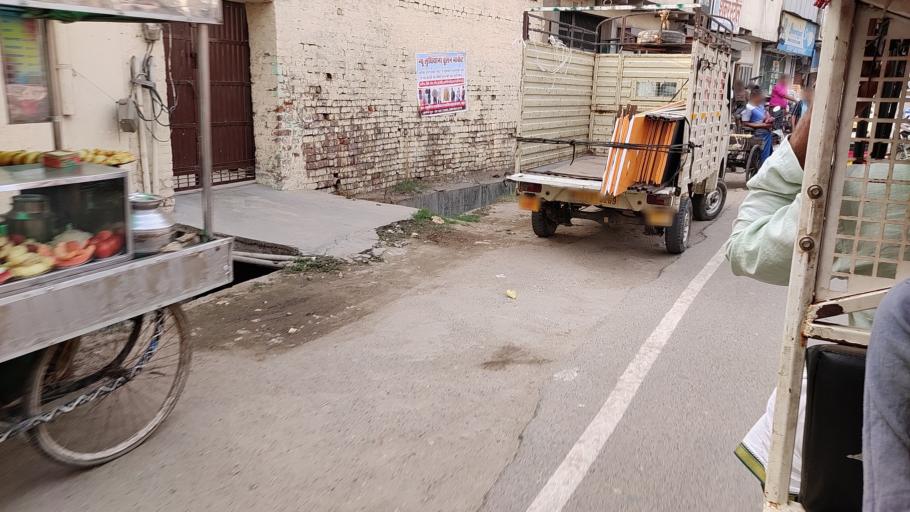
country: IN
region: Uttar Pradesh
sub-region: Mathura
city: Mathura
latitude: 27.5095
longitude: 77.6710
